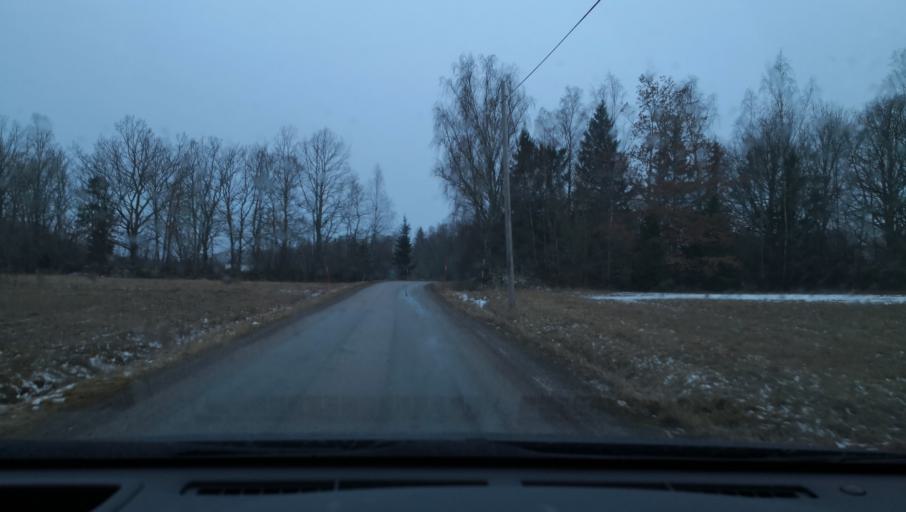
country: SE
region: Uppsala
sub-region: Enkopings Kommun
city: Hummelsta
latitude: 59.4549
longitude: 16.8243
